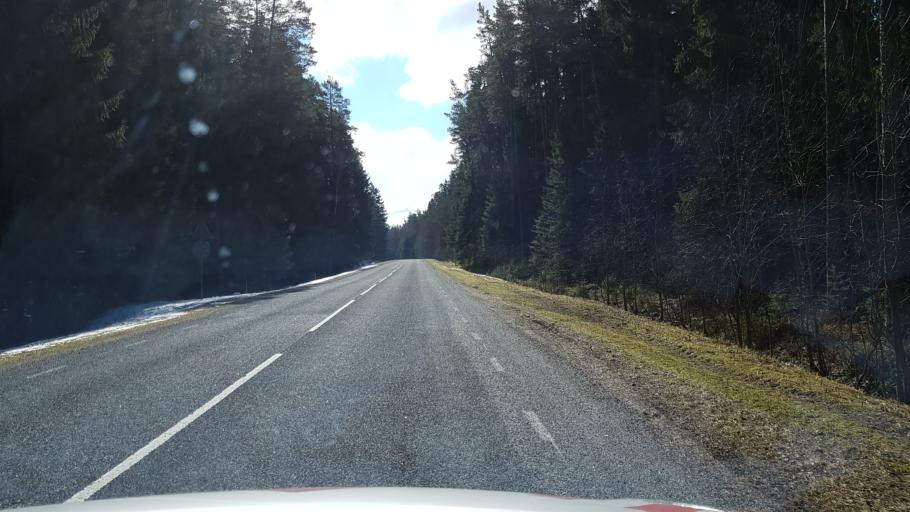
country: EE
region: Harju
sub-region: Loksa linn
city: Loksa
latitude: 59.5745
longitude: 25.9296
